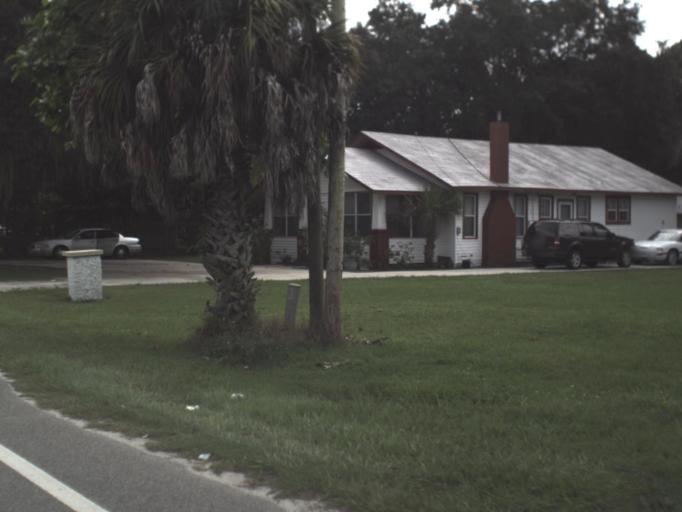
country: US
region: Florida
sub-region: Manatee County
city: Samoset
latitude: 27.4867
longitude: -82.5467
